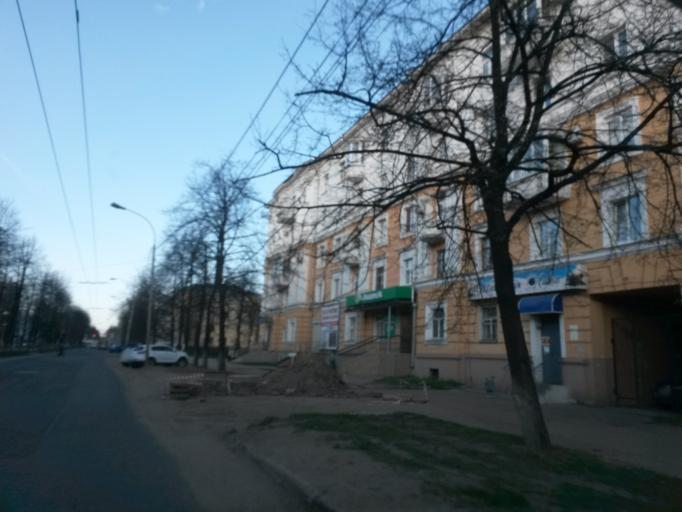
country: RU
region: Jaroslavl
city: Yaroslavl
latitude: 57.6343
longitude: 39.8612
